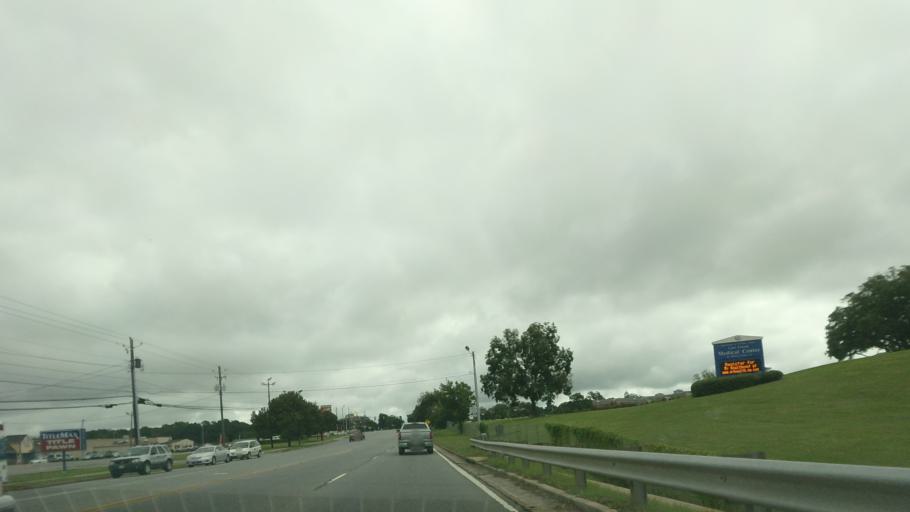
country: US
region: Georgia
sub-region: Laurens County
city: Dublin
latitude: 32.5405
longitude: -82.9464
